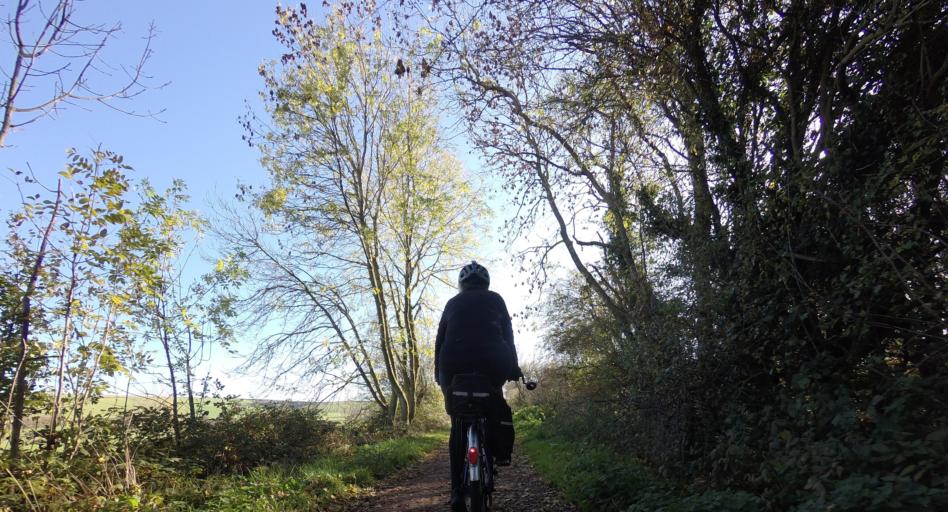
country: GB
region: England
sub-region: West Sussex
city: Steyning
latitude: 50.8760
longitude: -0.3084
